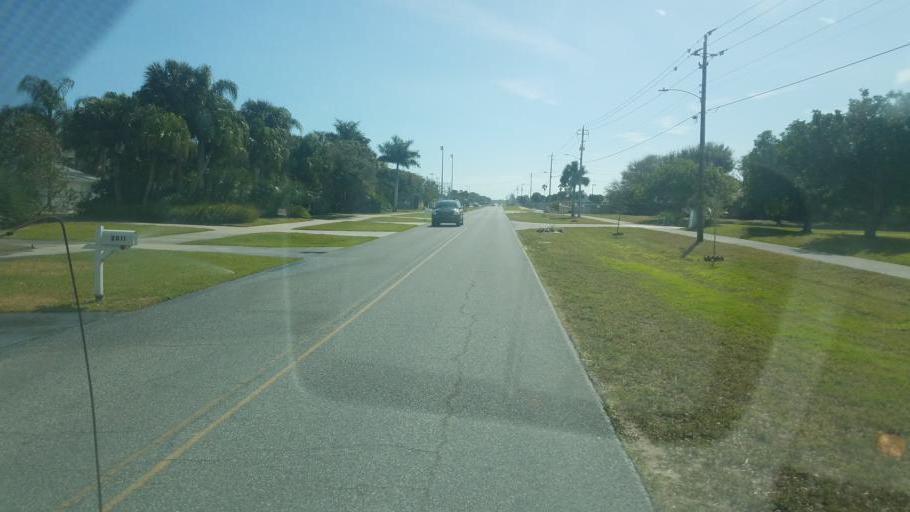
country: US
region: Florida
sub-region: Brevard County
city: Melbourne Beach
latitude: 28.0574
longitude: -80.5578
